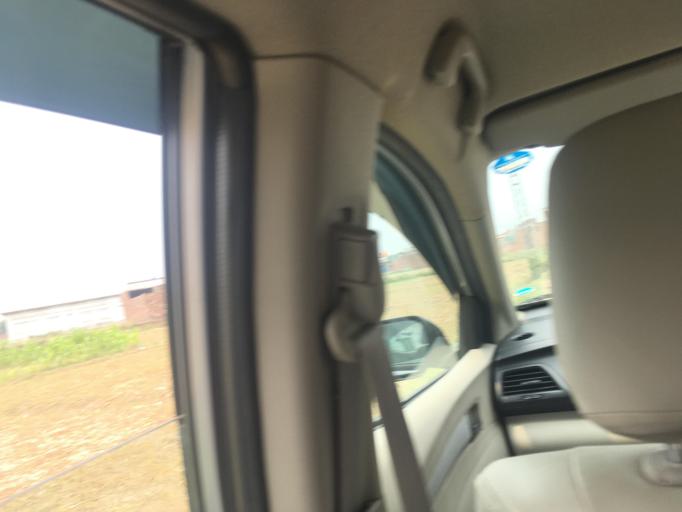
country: PK
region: Punjab
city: Lahore
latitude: 31.6151
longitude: 74.3545
